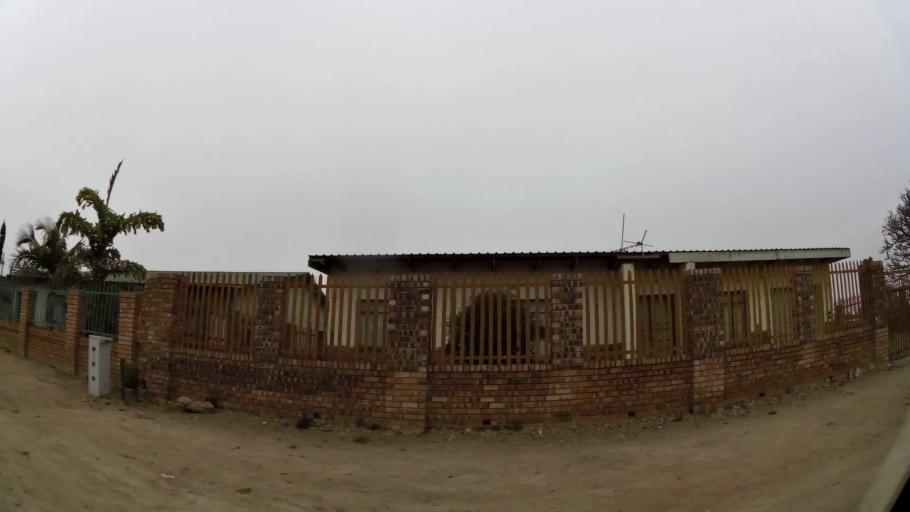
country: ZA
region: Limpopo
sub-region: Capricorn District Municipality
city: Polokwane
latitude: -23.8514
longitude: 29.3918
